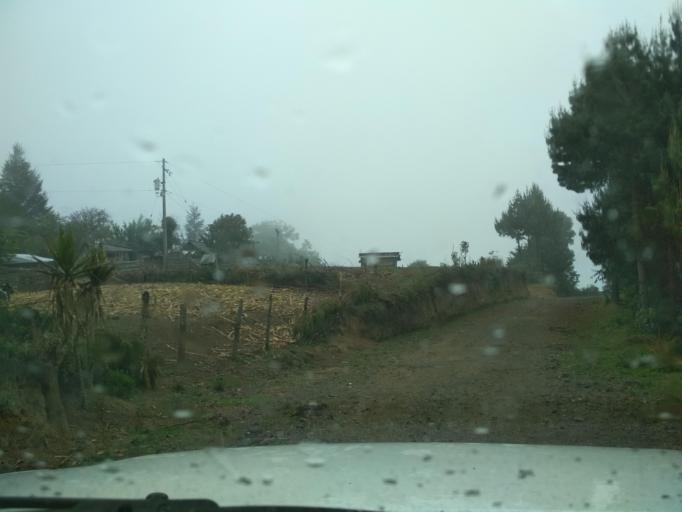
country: MX
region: Veracruz
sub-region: Mariano Escobedo
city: Loma Grande
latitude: 18.9289
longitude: -97.2201
